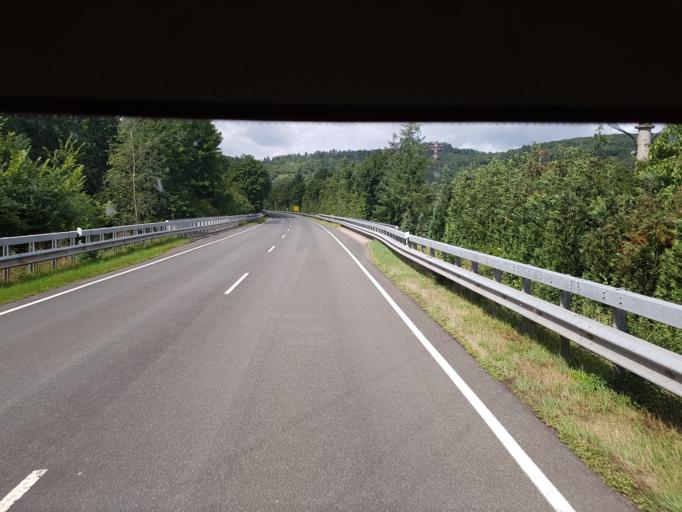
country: DE
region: Rheinland-Pfalz
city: Punderich
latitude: 50.0382
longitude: 7.1286
